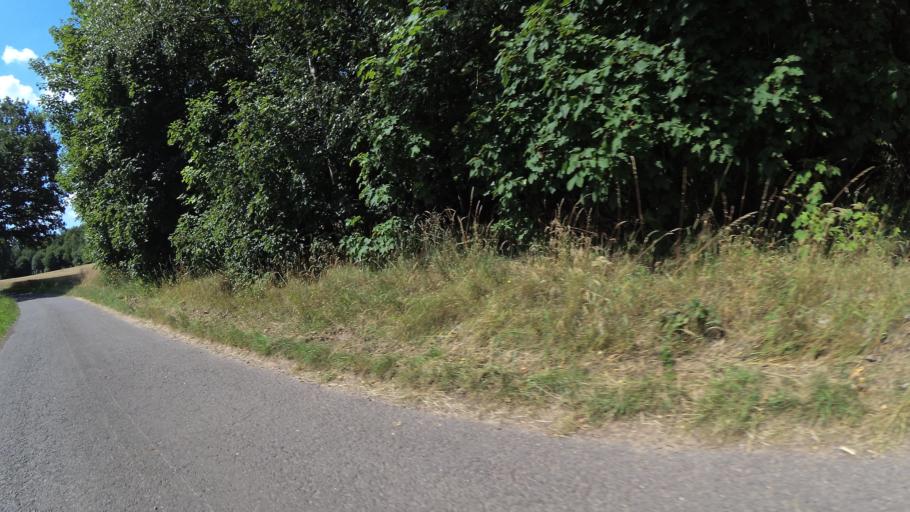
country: DE
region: Saarland
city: Weiskirchen
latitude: 49.5136
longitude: 6.8218
